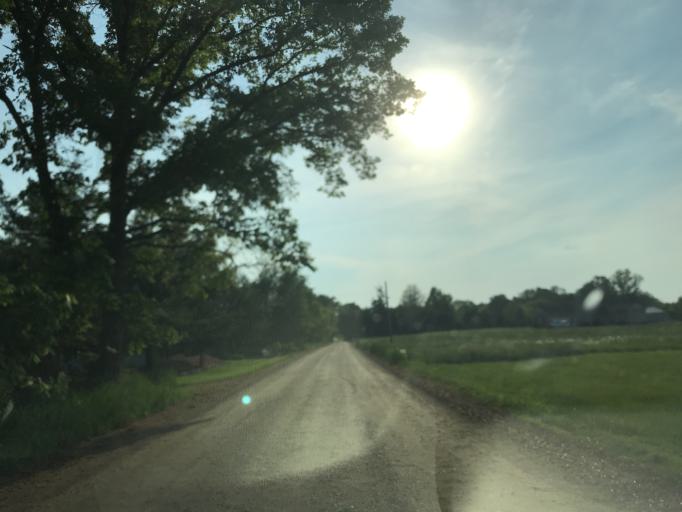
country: US
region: Michigan
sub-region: Oakland County
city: South Lyon
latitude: 42.4868
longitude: -83.6276
